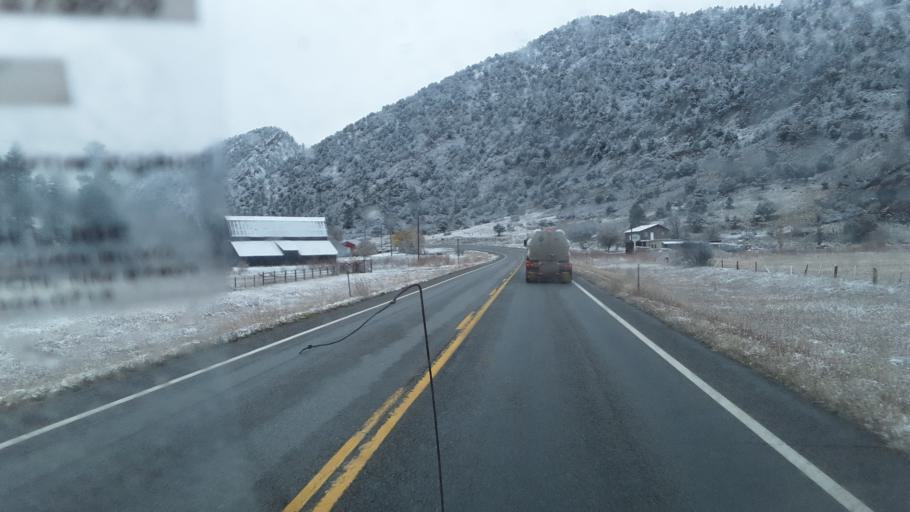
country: US
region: Colorado
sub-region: La Plata County
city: Bayfield
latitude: 37.2266
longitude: -107.3450
